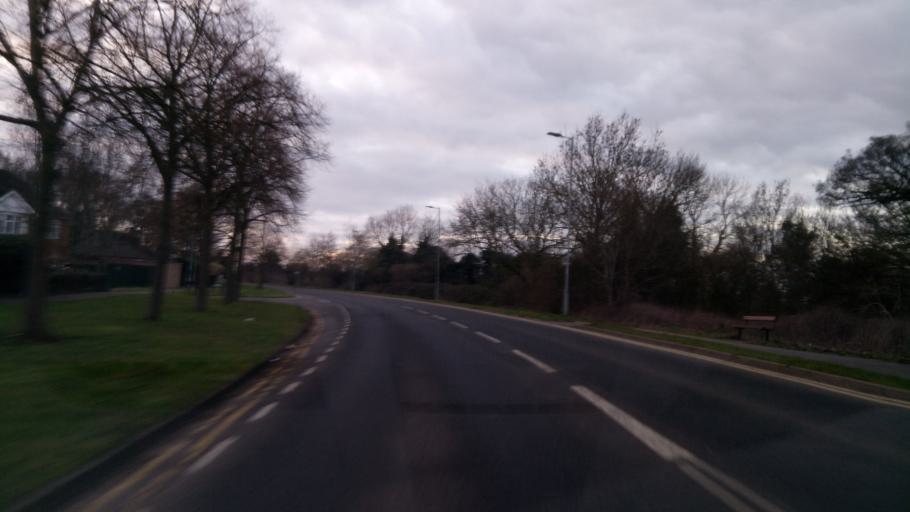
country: GB
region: England
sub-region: Peterborough
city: Peterborough
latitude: 52.5590
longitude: -0.2324
